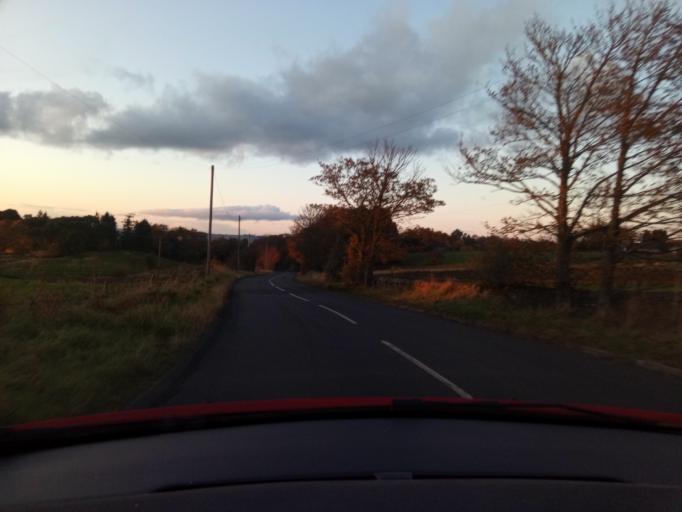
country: GB
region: England
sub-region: Northumberland
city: Bardon Mill
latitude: 54.9423
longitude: -2.2667
